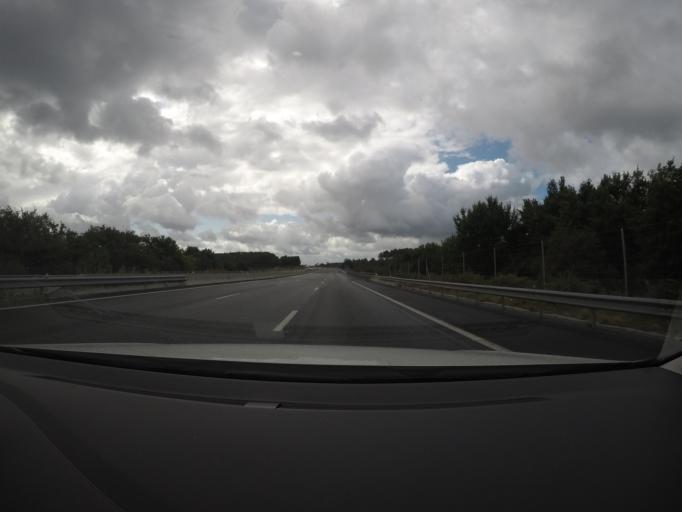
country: FR
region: Aquitaine
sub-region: Departement de la Gironde
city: Salles
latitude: 44.5164
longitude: -0.8403
